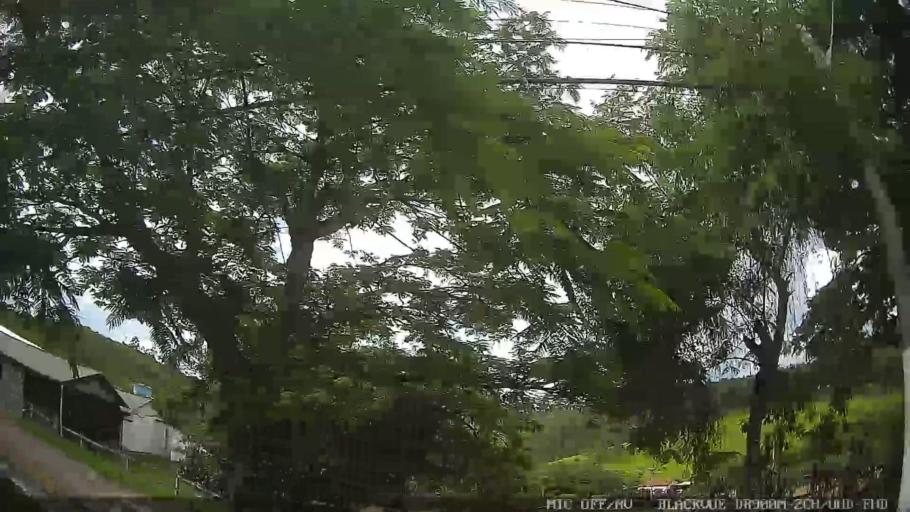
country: BR
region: Sao Paulo
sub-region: Santa Branca
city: Santa Branca
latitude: -23.5242
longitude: -45.8612
